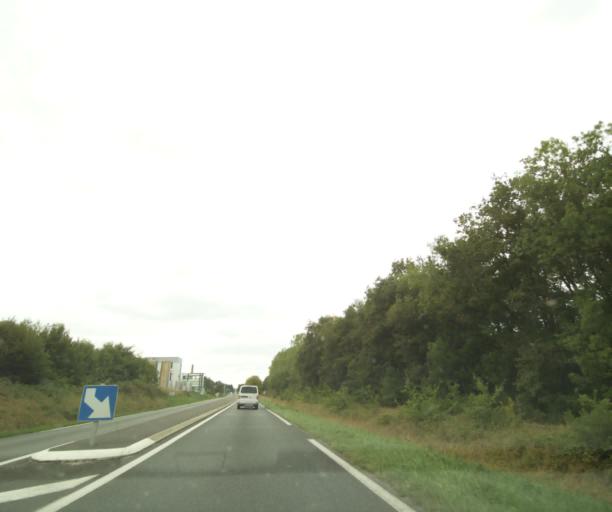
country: FR
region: Centre
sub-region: Departement d'Indre-et-Loire
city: Perrusson
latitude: 47.0745
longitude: 1.0654
